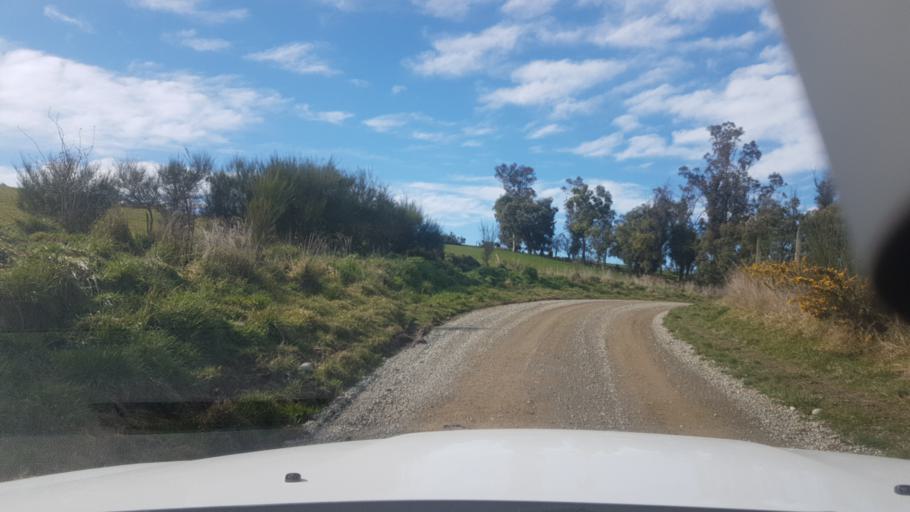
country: NZ
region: Canterbury
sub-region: Timaru District
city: Pleasant Point
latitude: -44.2031
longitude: 171.1951
